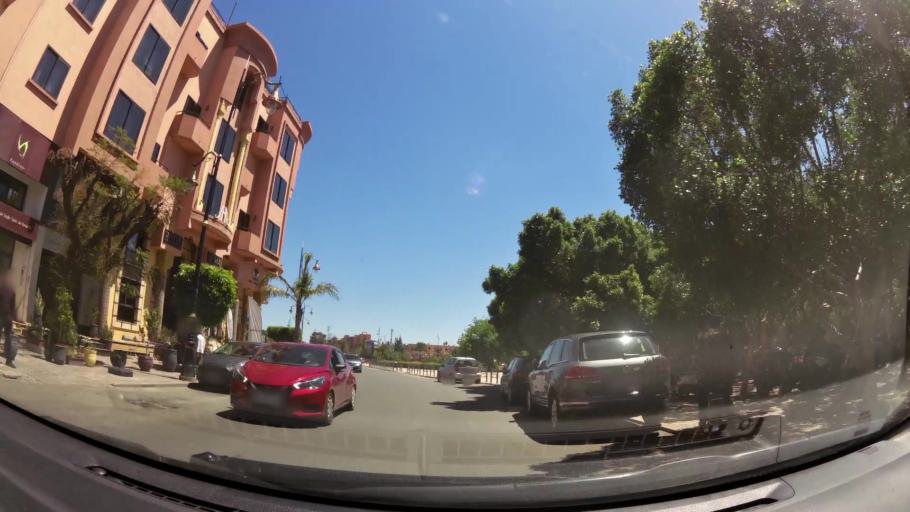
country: MA
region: Marrakech-Tensift-Al Haouz
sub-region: Marrakech
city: Marrakesh
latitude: 31.6269
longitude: -8.0157
